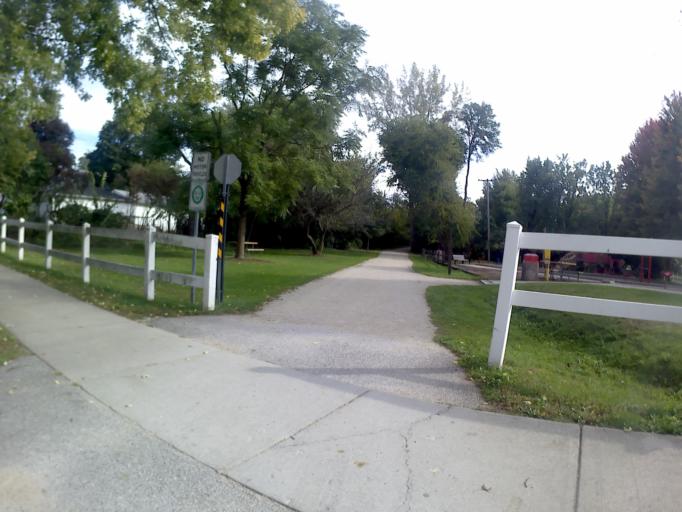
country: US
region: Illinois
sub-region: DuPage County
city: Wheaton
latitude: 41.8700
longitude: -88.1177
